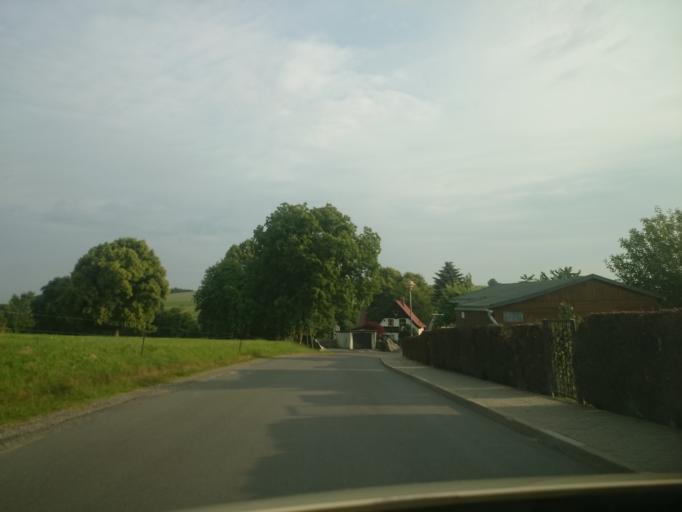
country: DE
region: Saxony
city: Leubsdorf
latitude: 50.7978
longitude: 13.1656
